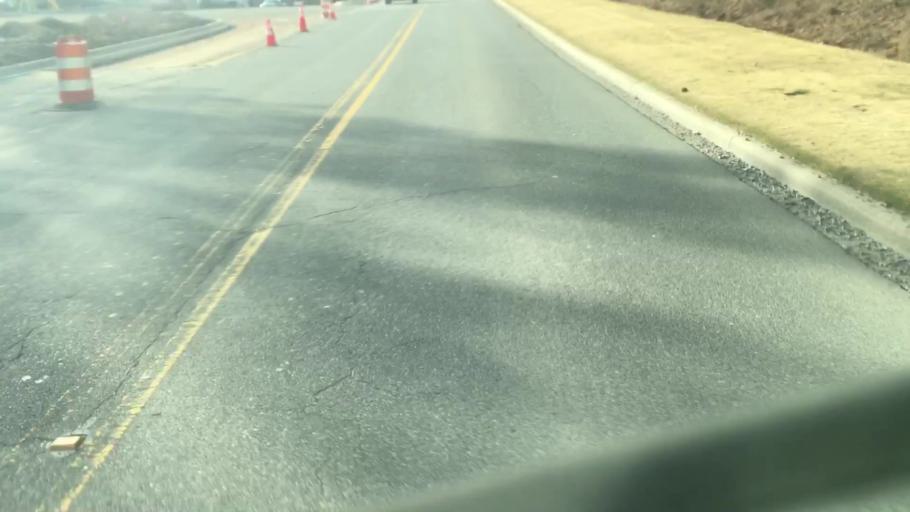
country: US
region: Alabama
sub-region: Jefferson County
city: Cahaba Heights
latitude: 33.4745
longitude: -86.7003
